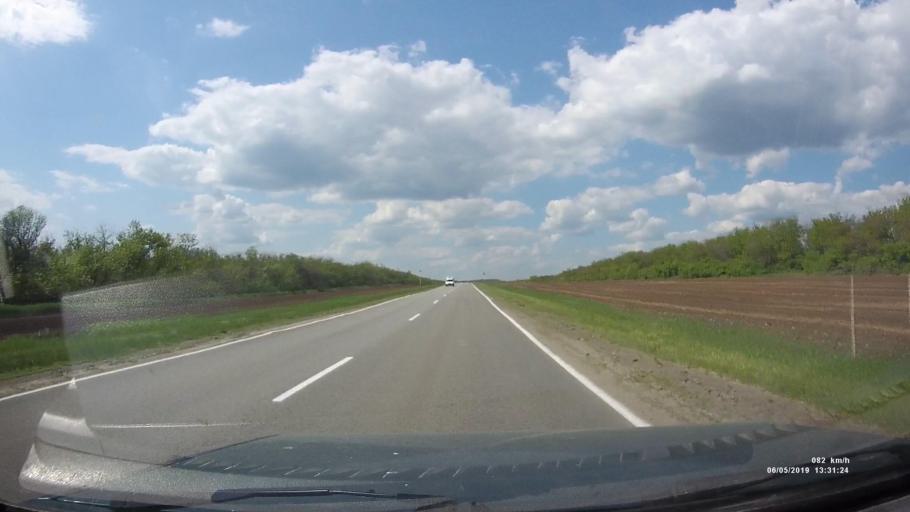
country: RU
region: Rostov
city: Ust'-Donetskiy
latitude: 47.6765
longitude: 40.8111
